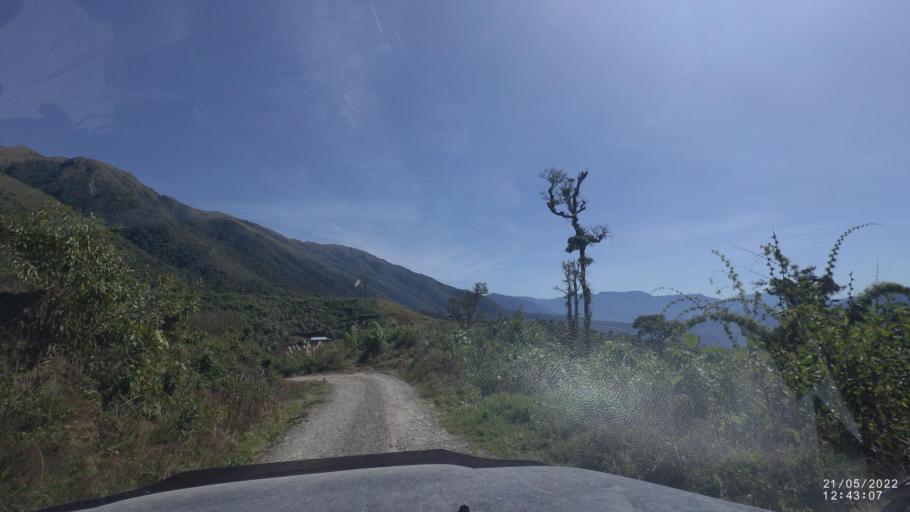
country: BO
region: Cochabamba
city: Colomi
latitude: -17.1909
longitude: -65.9319
